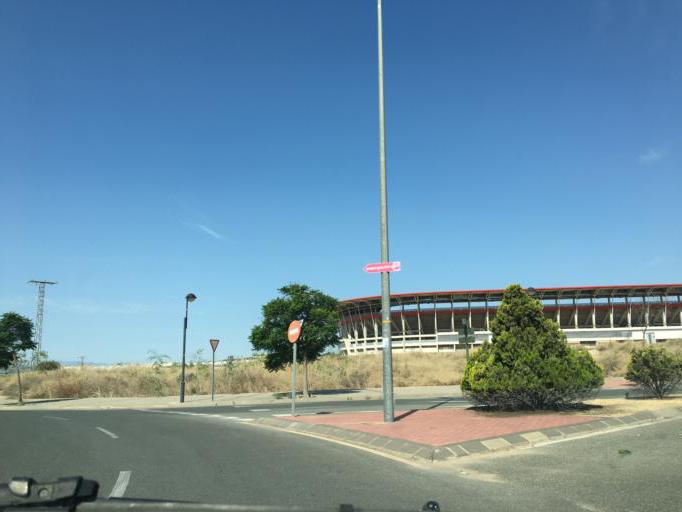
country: ES
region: Murcia
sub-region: Murcia
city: Murcia
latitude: 38.0414
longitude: -1.1412
